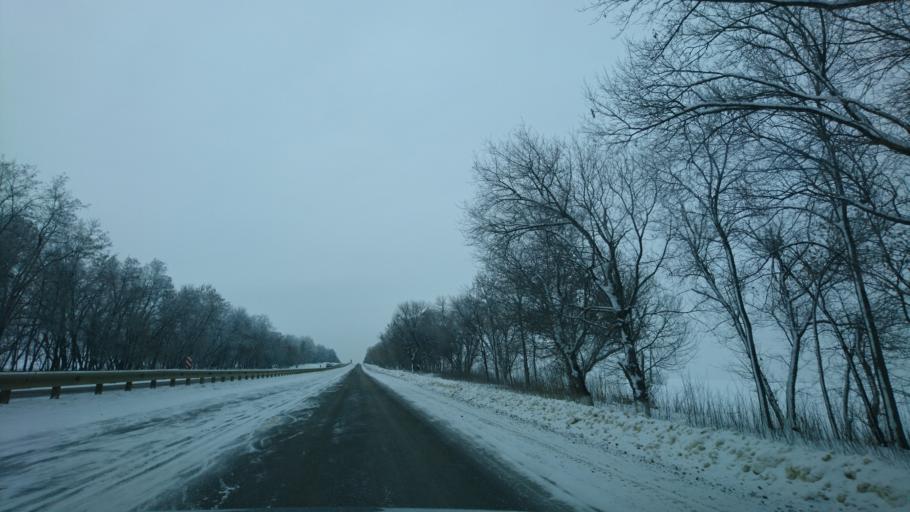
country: RU
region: Belgorod
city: Mayskiy
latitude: 50.4247
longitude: 36.3808
